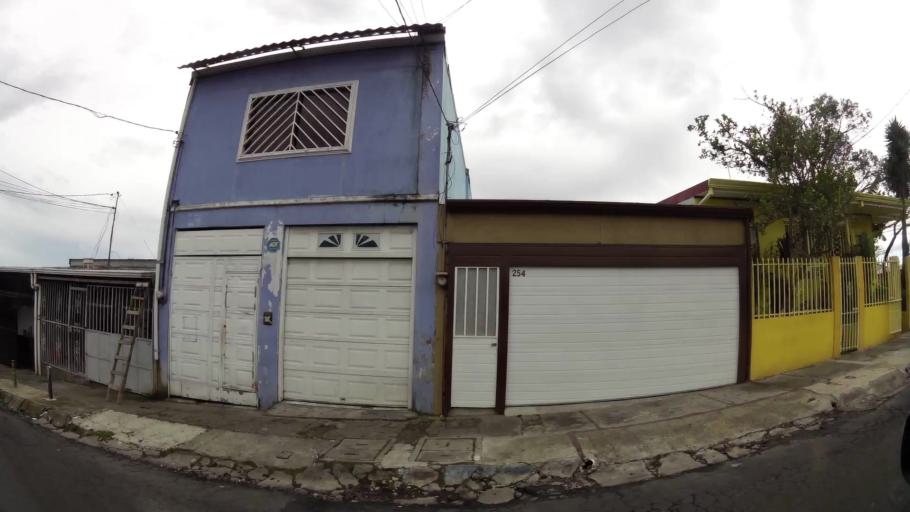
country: CR
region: San Jose
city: Purral
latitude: 9.9623
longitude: -84.0234
